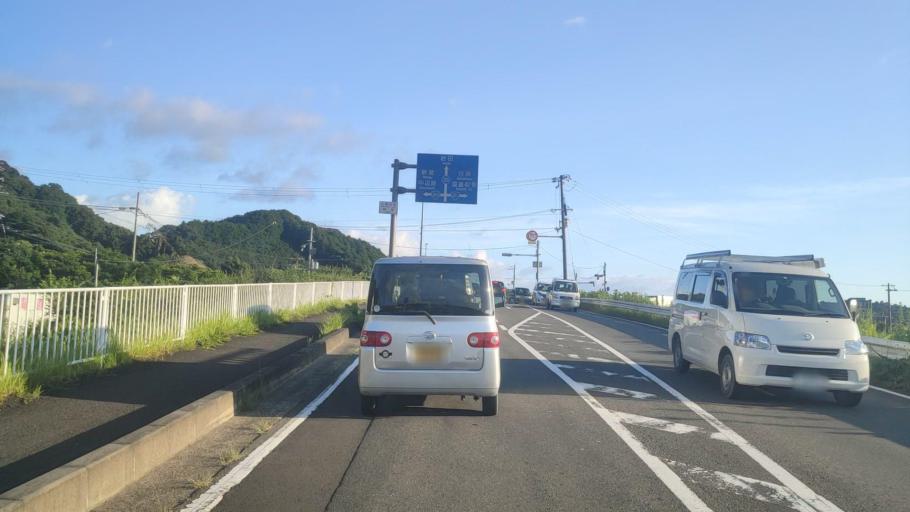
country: JP
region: Wakayama
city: Tanabe
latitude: 33.7143
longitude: 135.4473
